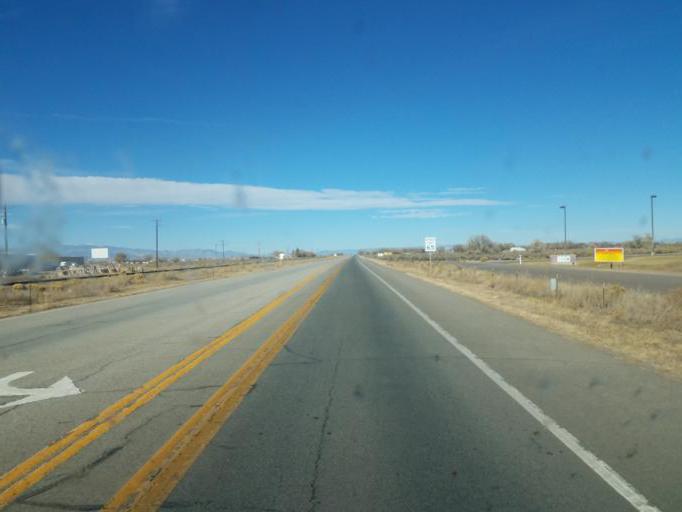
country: US
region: Colorado
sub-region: Alamosa County
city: Alamosa
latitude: 37.4911
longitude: -105.9318
